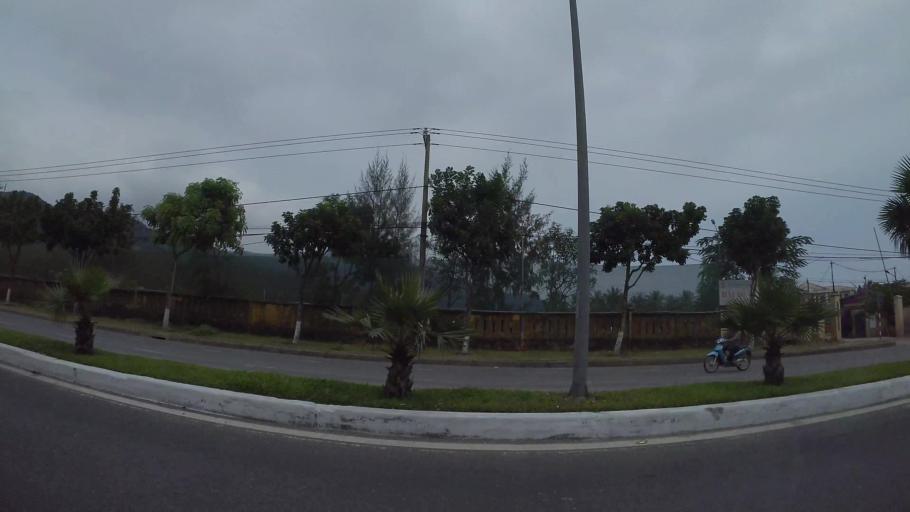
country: VN
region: Da Nang
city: Da Nang
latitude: 16.1034
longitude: 108.2473
